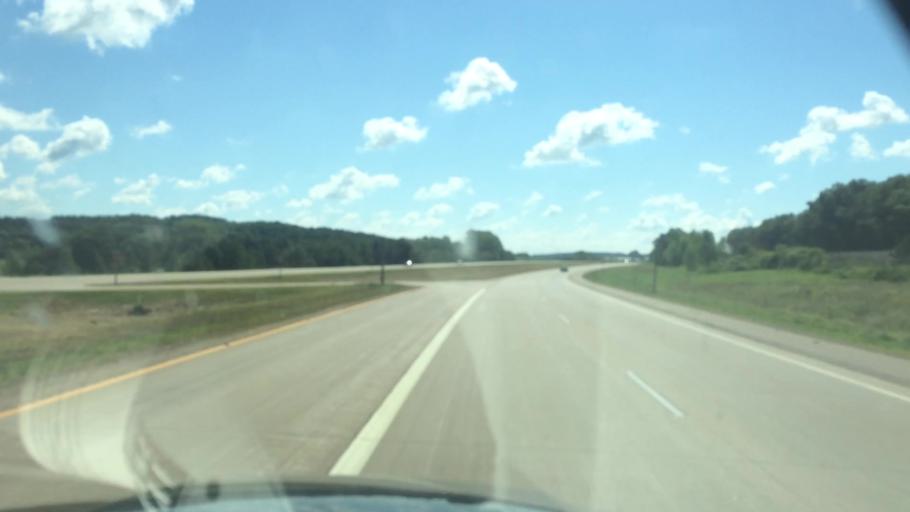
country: US
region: Wisconsin
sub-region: Portage County
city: Amherst
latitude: 44.5011
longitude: -89.3828
